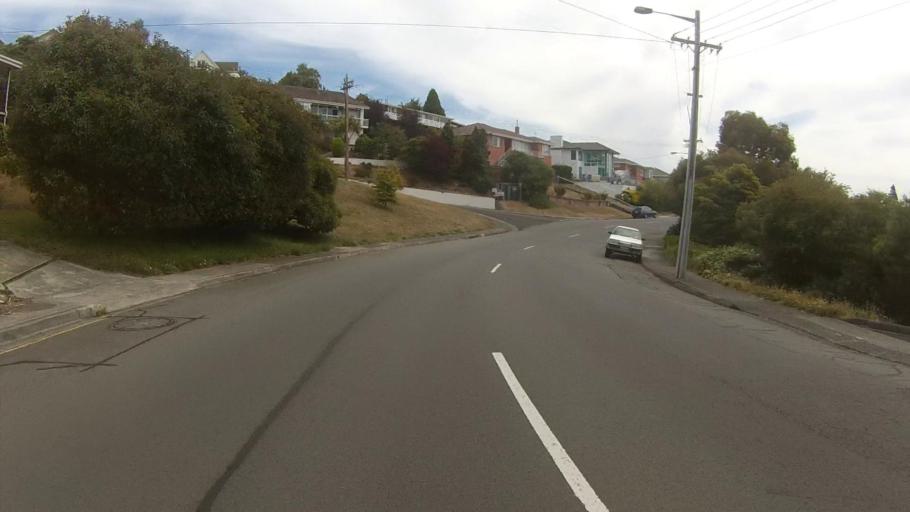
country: AU
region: Tasmania
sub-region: Hobart
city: Sandy Bay
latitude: -42.9156
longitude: 147.3440
